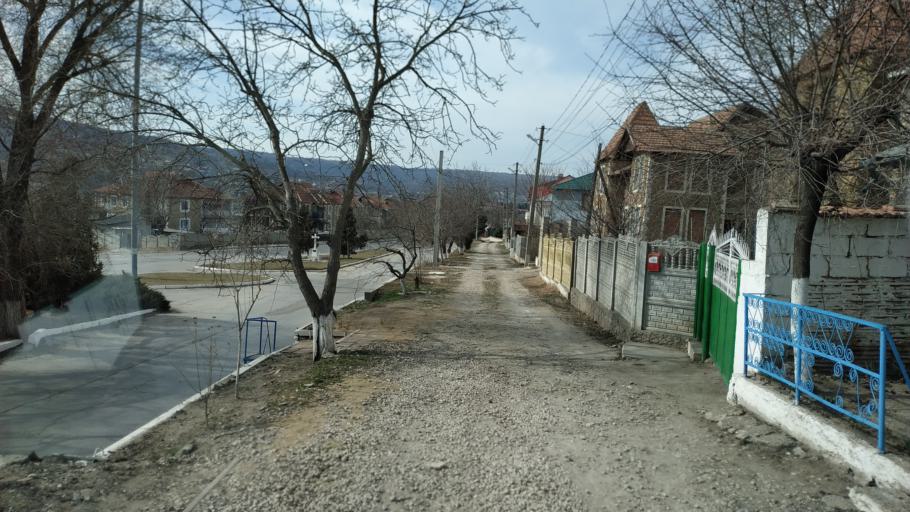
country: MD
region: Chisinau
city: Vatra
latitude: 47.0942
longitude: 28.6737
